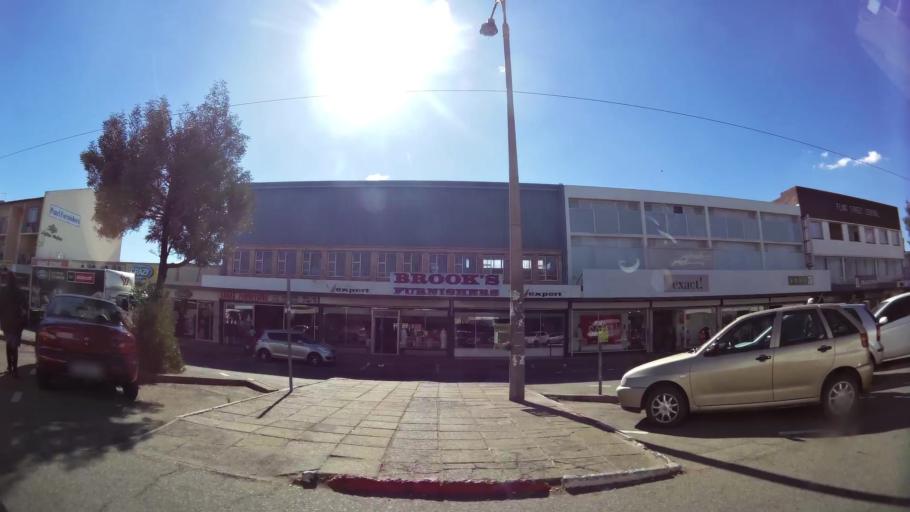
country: ZA
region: Gauteng
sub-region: West Rand District Municipality
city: Carletonville
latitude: -26.3569
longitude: 27.3986
